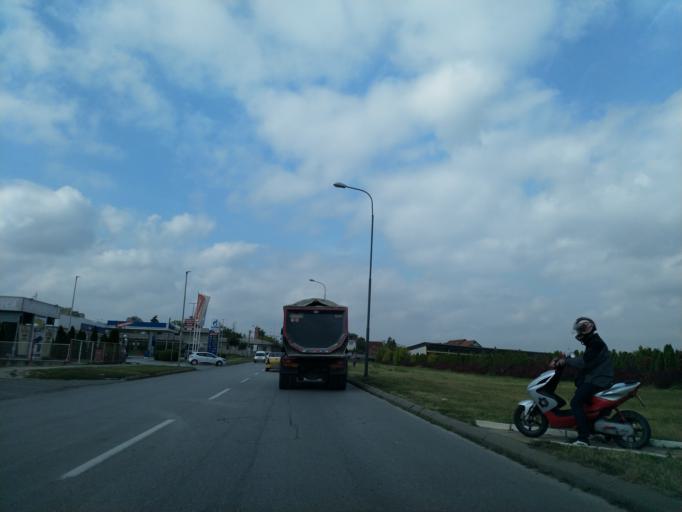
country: RS
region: Central Serbia
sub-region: Sumadijski Okrug
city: Kragujevac
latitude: 44.0281
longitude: 20.9197
